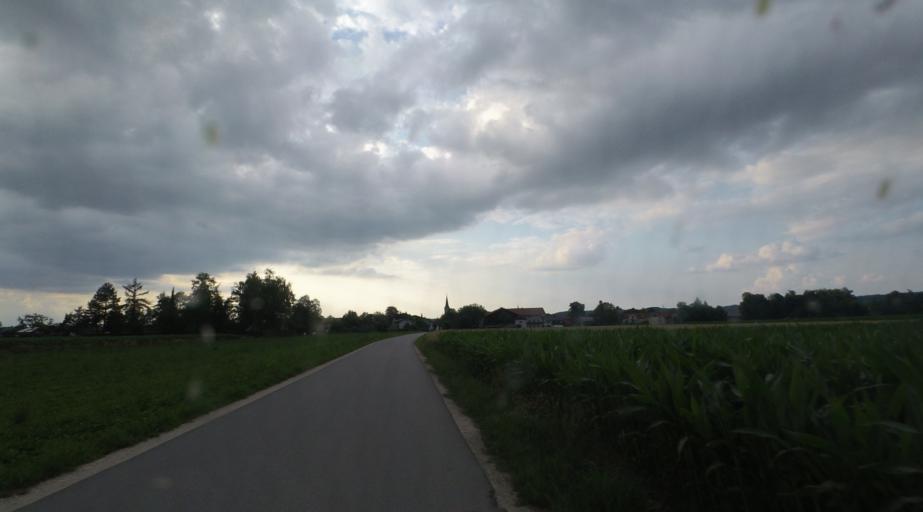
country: DE
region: Bavaria
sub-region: Upper Bavaria
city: Grabenstatt
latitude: 47.8392
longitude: 12.5435
